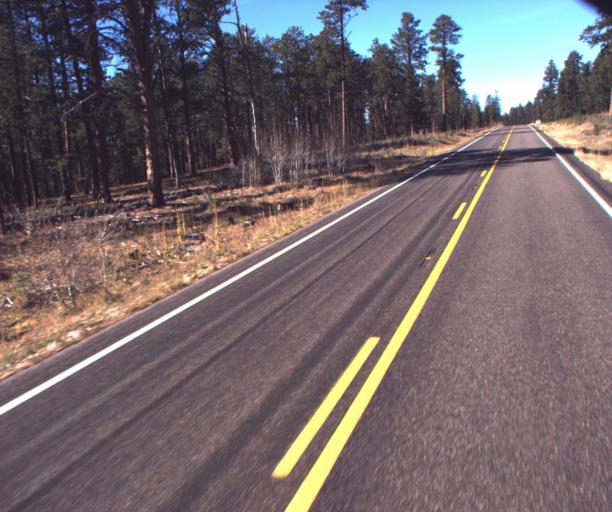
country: US
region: Arizona
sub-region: Coconino County
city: Fredonia
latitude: 36.6402
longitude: -112.1734
